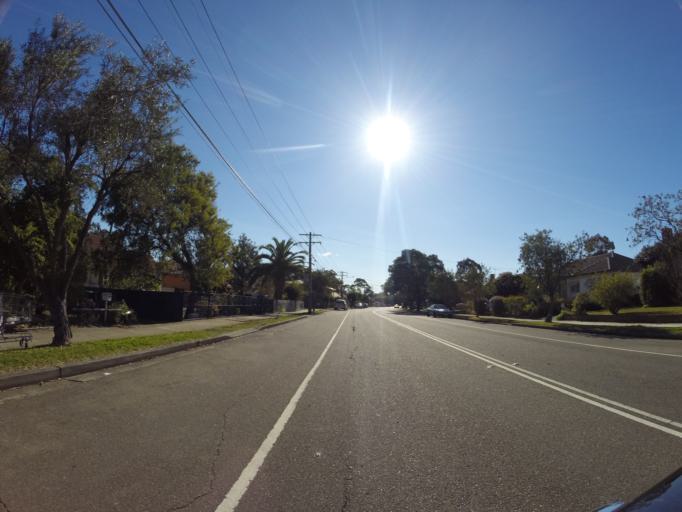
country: AU
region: New South Wales
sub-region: Auburn
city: Lidcombe
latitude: -33.8557
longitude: 151.0423
